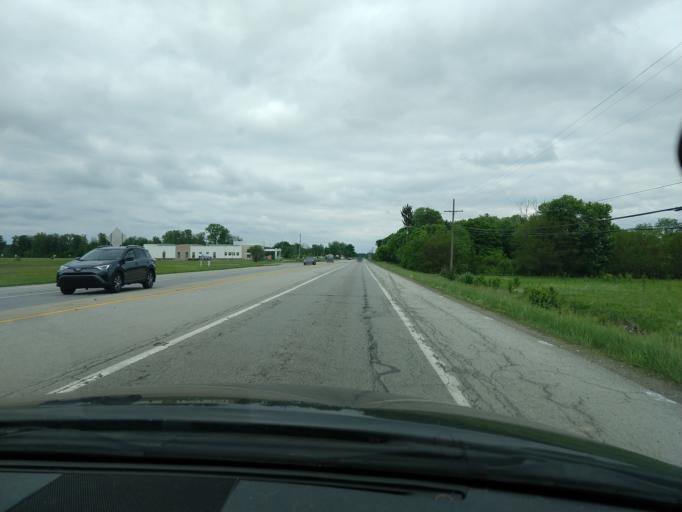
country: US
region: Indiana
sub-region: Hamilton County
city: Westfield
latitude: 40.0432
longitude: -86.0681
